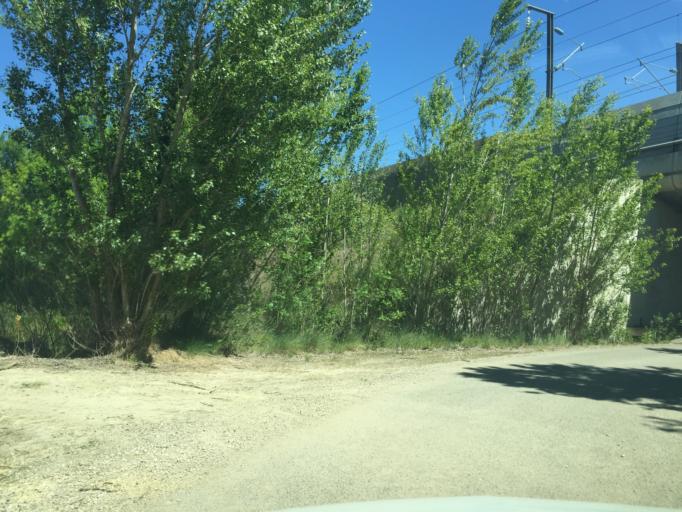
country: FR
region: Provence-Alpes-Cote d'Azur
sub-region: Departement du Vaucluse
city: Caderousse
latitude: 44.0866
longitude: 4.7717
